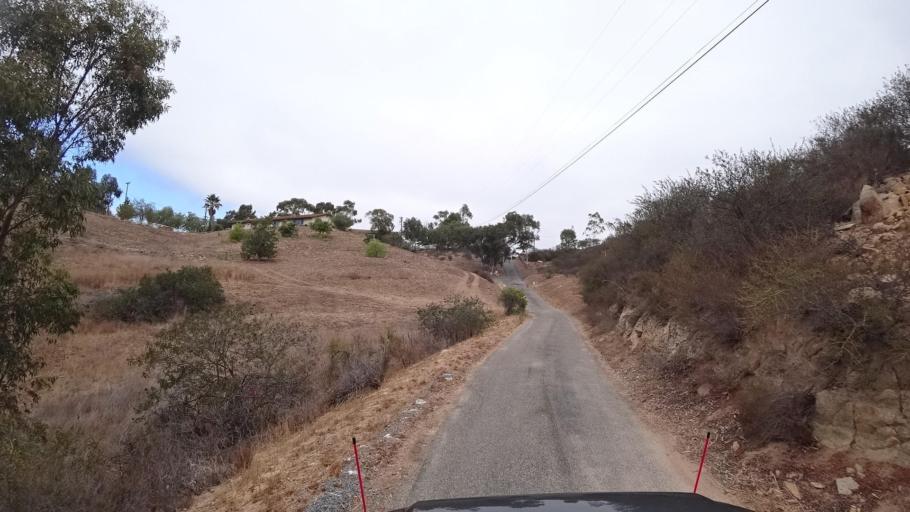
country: US
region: California
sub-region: San Diego County
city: Fallbrook
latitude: 33.4356
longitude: -117.3130
